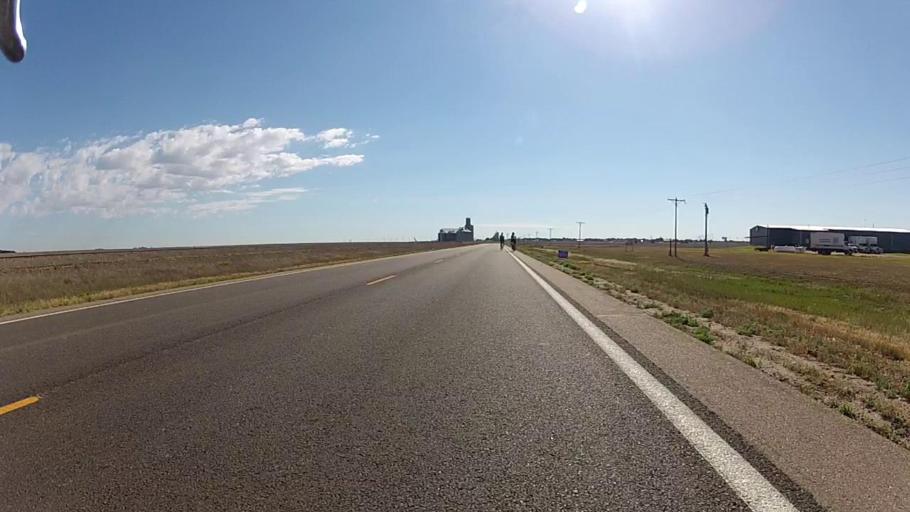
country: US
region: Kansas
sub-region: Gray County
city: Cimarron
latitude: 37.5924
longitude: -100.4674
